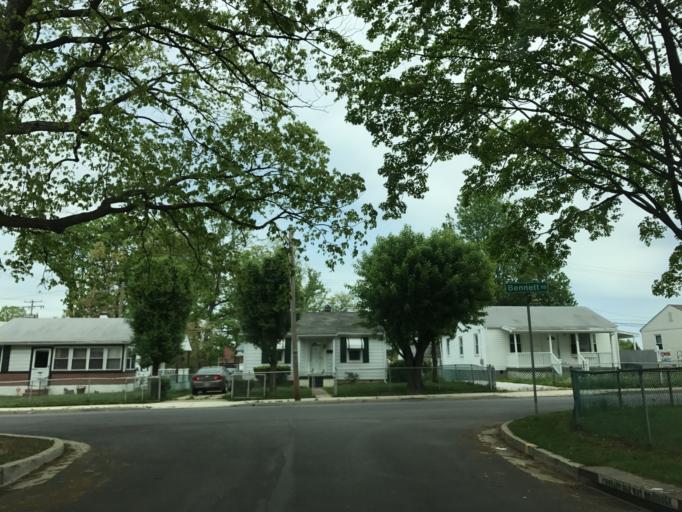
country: US
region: Maryland
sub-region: Baltimore County
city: Middle River
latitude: 39.3243
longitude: -76.4518
